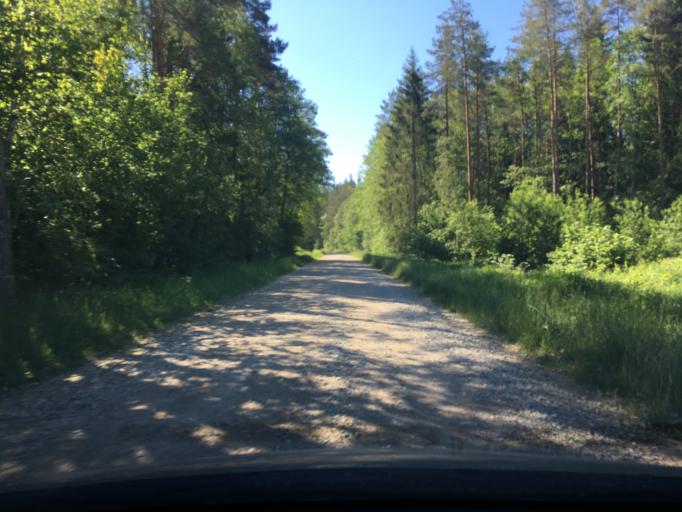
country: EE
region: Laeaene
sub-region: Lihula vald
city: Lihula
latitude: 58.6402
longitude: 23.7904
